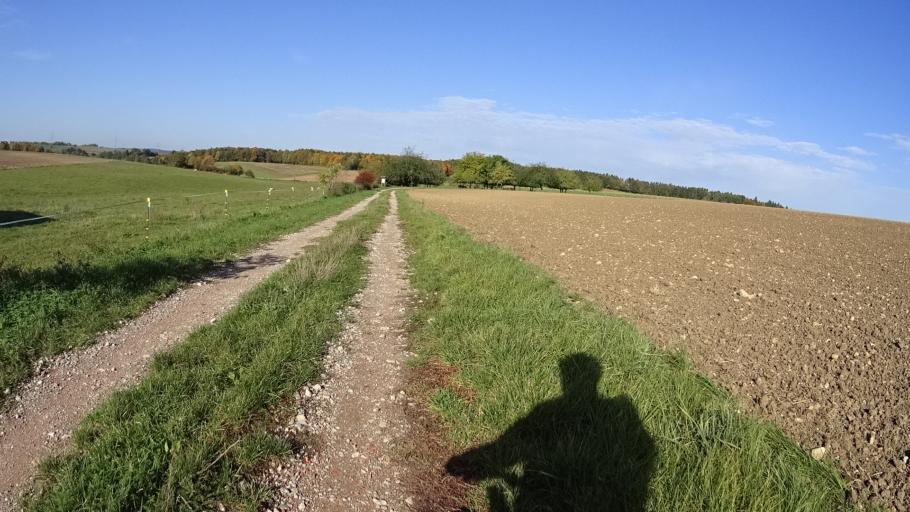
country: DE
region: Bavaria
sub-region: Upper Bavaria
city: Bohmfeld
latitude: 48.8670
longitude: 11.3648
